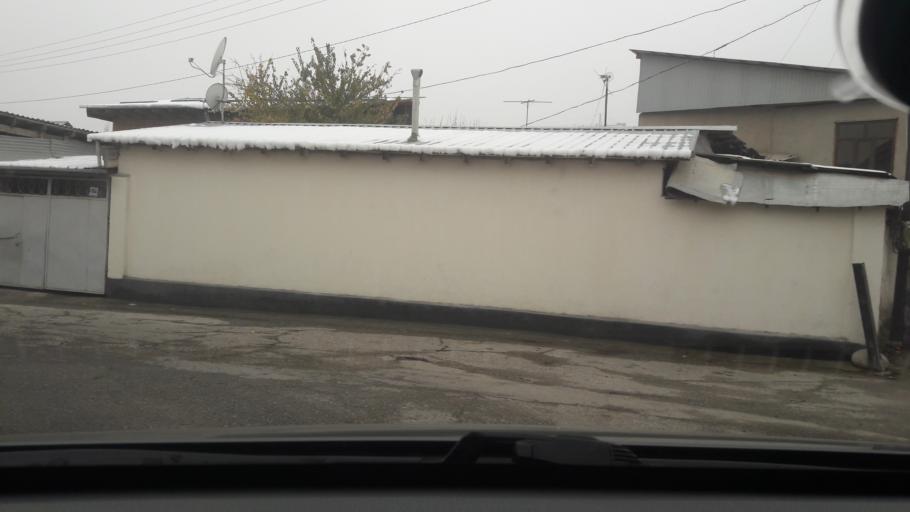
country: TJ
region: Dushanbe
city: Dushanbe
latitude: 38.5896
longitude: 68.7465
